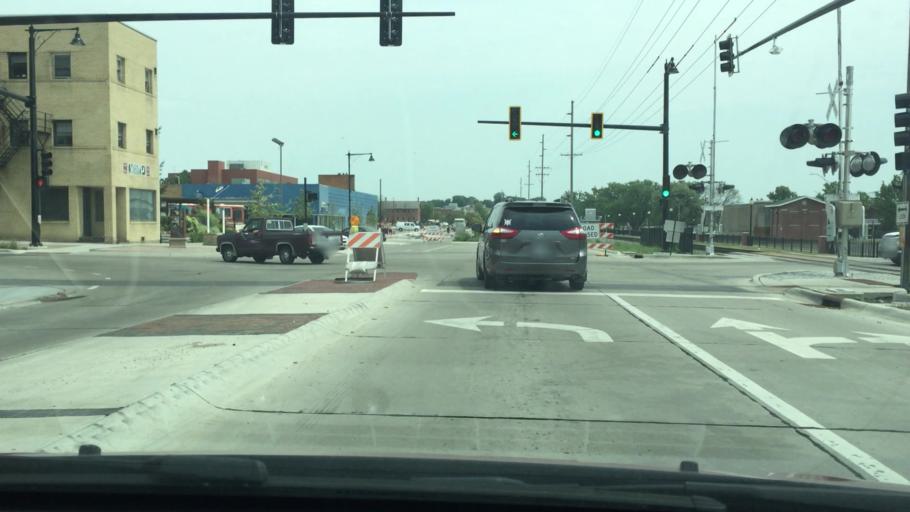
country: US
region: Iowa
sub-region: Muscatine County
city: Muscatine
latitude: 41.4203
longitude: -91.0452
